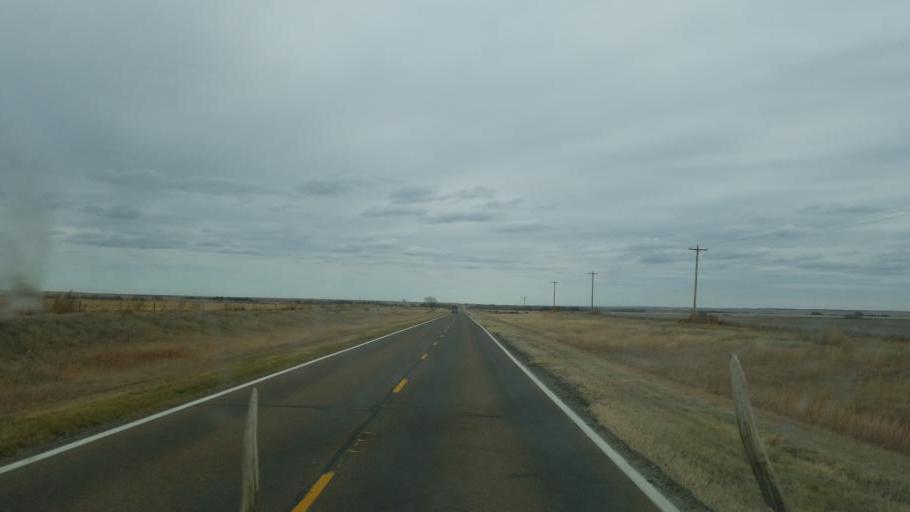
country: US
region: Kansas
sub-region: Wallace County
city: Sharon Springs
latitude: 38.9020
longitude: -101.7217
